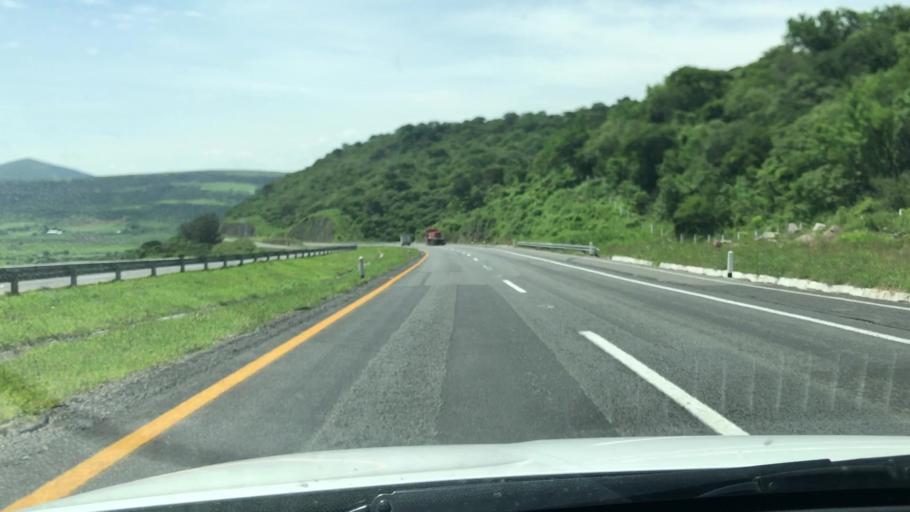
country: MX
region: Jalisco
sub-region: Zapotlan del Rey
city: Zapotlan del Rey
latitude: 20.5092
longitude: -102.9682
